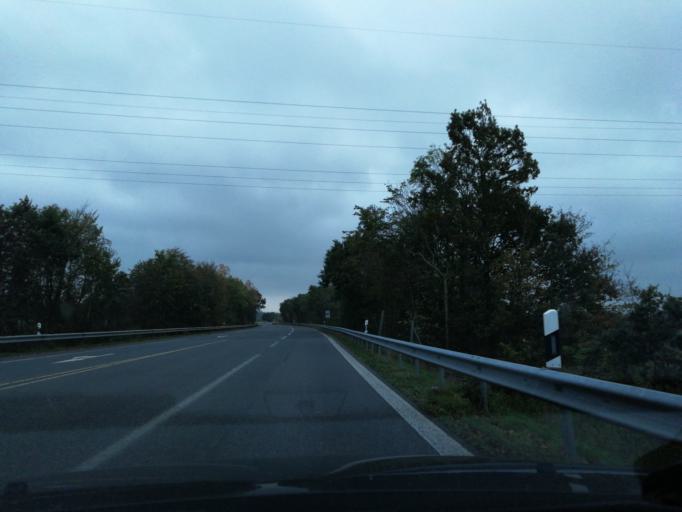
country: DE
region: Lower Saxony
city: Fedderwarden
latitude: 53.5444
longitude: 8.0500
